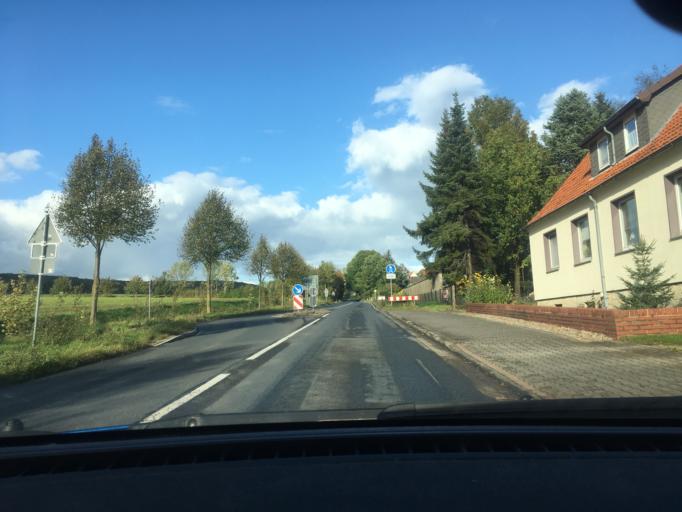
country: DE
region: Lower Saxony
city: Weenzen
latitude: 52.0228
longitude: 9.6723
